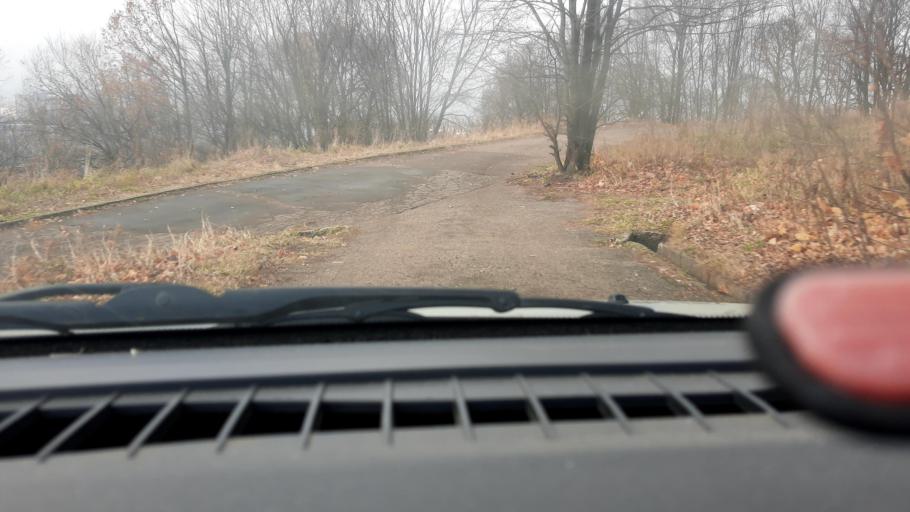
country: RU
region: Nizjnij Novgorod
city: Nizhniy Novgorod
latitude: 56.2967
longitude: 43.9714
